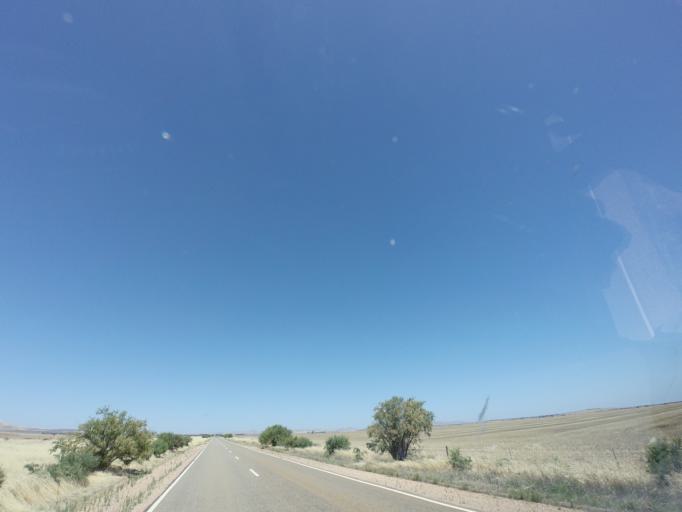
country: AU
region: South Australia
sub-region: Flinders Ranges
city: Quorn
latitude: -32.6893
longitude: 138.3392
